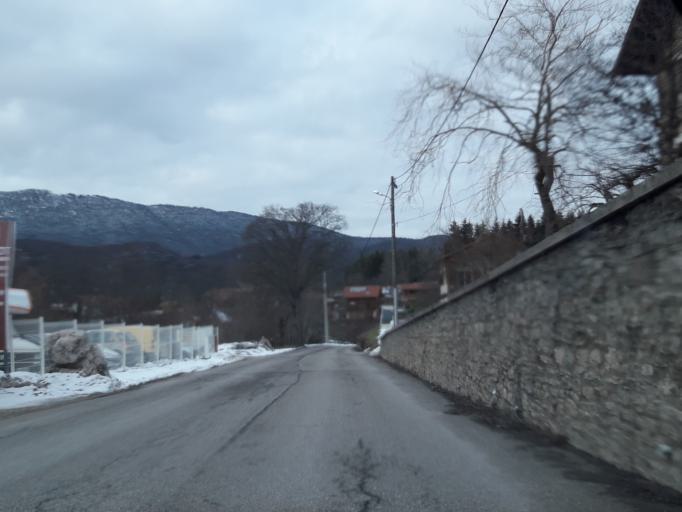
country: FR
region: Rhone-Alpes
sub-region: Departement de la Drome
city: Saint-Laurent-en-Royans
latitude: 44.9686
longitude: 5.4120
